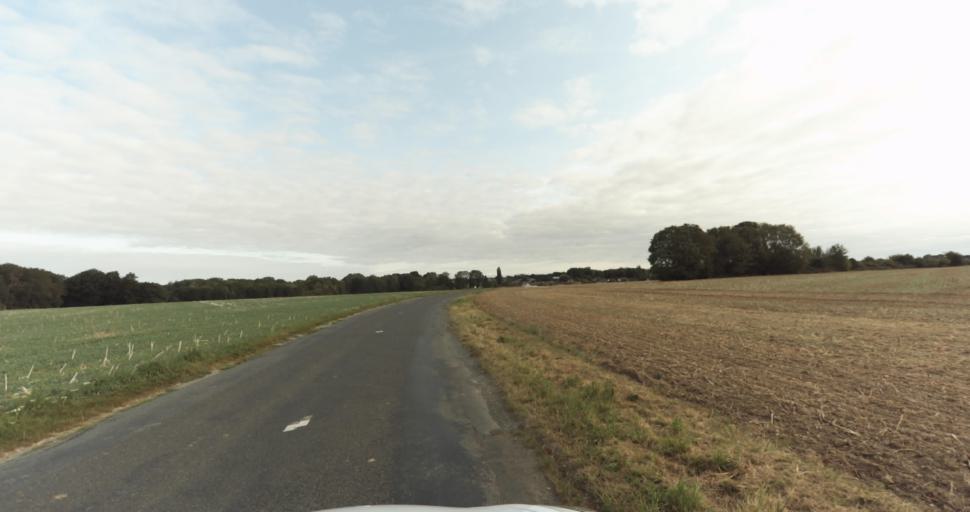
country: FR
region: Haute-Normandie
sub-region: Departement de l'Eure
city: Saint-Germain-sur-Avre
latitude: 48.8127
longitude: 1.2662
